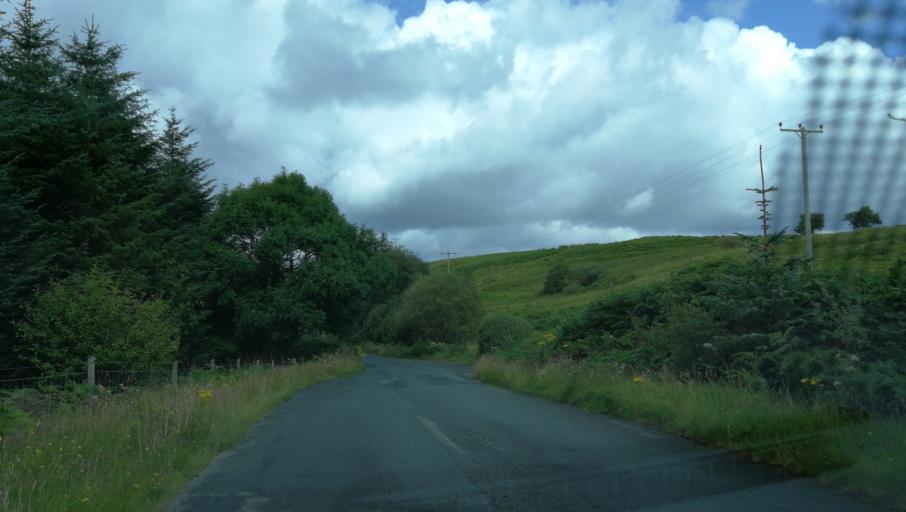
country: GB
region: Scotland
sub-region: Highland
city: Portree
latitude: 57.3818
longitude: -6.1945
